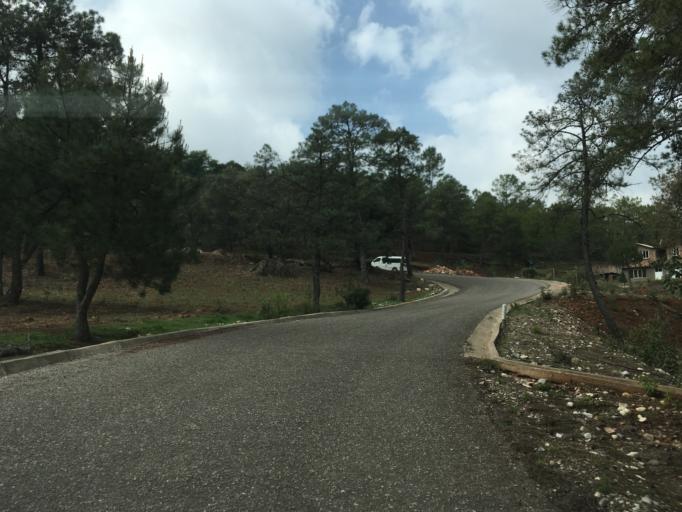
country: MX
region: Oaxaca
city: Santiago Tilantongo
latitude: 17.2197
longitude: -97.2793
